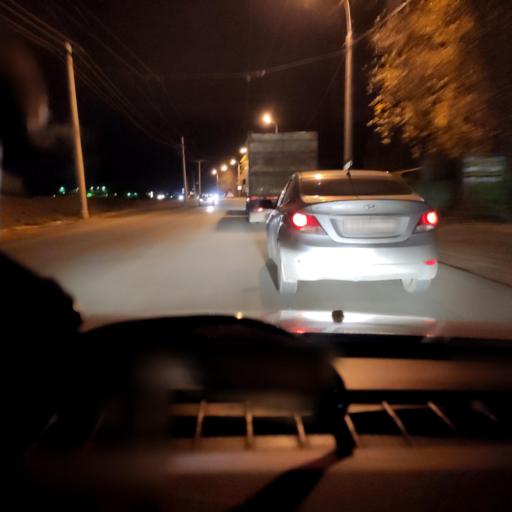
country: RU
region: Samara
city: Samara
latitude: 53.1440
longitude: 50.0973
